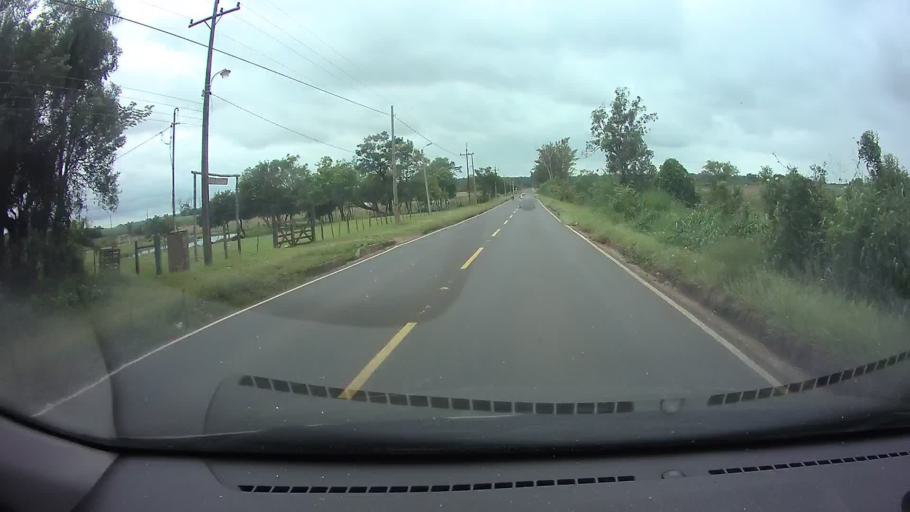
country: PY
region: Central
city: Nueva Italia
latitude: -25.6104
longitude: -57.4587
